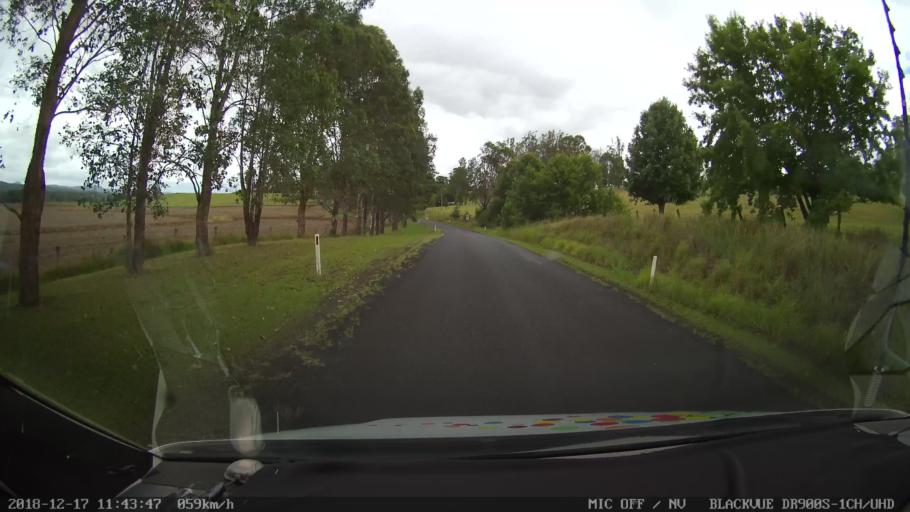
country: AU
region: New South Wales
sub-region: Kyogle
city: Kyogle
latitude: -28.6572
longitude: 152.5941
